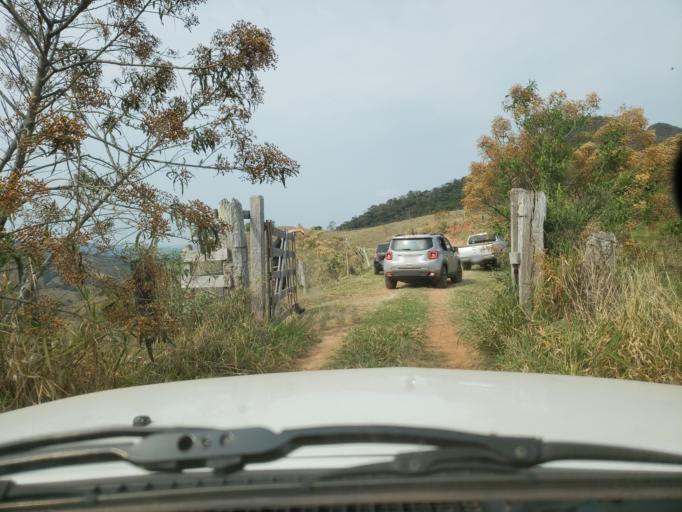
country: BR
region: Minas Gerais
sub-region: Jacutinga
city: Jacutinga
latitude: -22.3420
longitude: -46.5857
